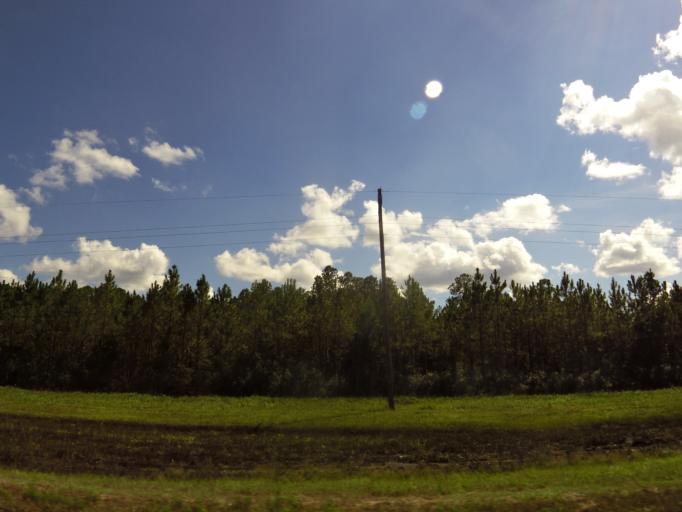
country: US
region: Florida
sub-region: Hamilton County
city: Jasper
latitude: 30.6775
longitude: -82.6203
